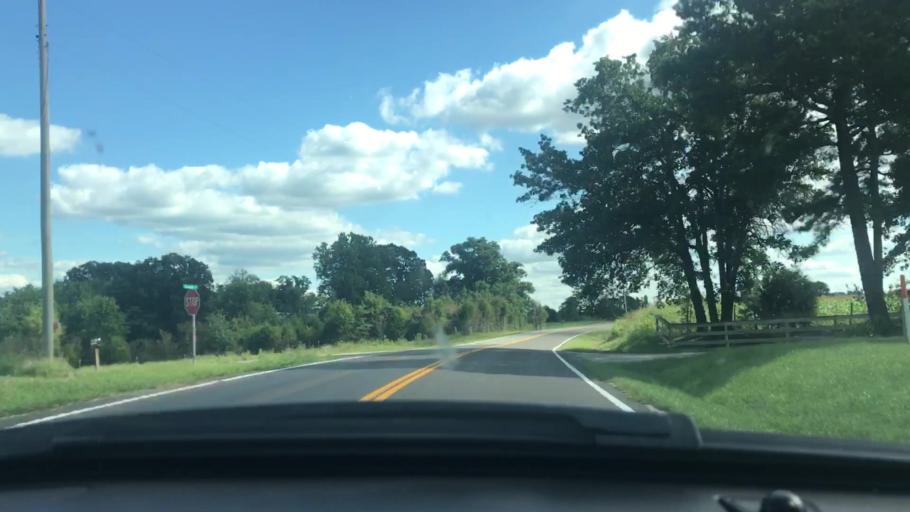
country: US
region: Missouri
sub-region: Wright County
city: Mountain Grove
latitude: 37.1766
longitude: -92.2672
